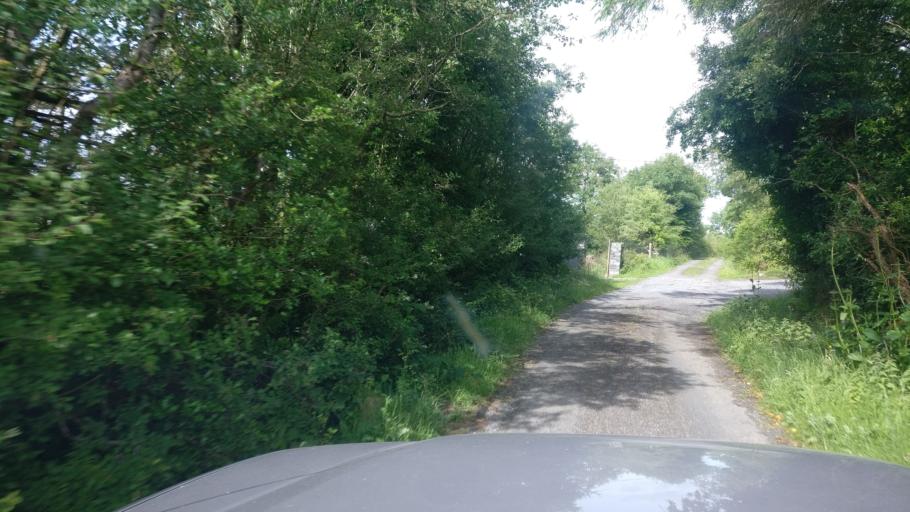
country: IE
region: Connaught
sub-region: County Galway
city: Gort
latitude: 53.0994
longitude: -8.6927
